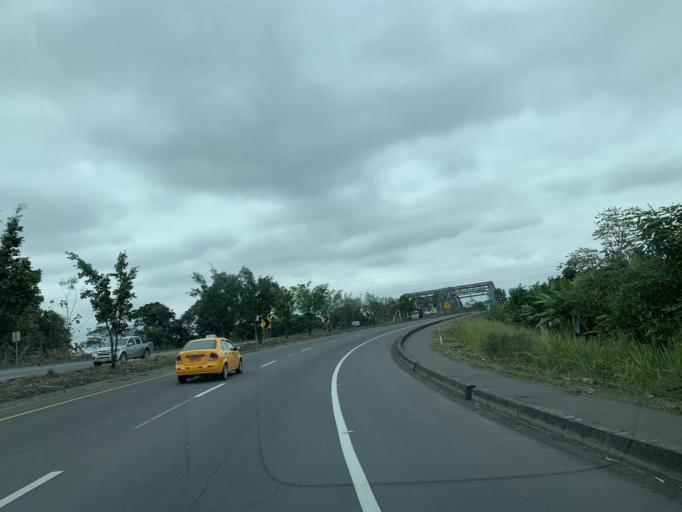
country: EC
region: Canar
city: La Troncal
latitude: -2.3567
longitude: -79.3932
